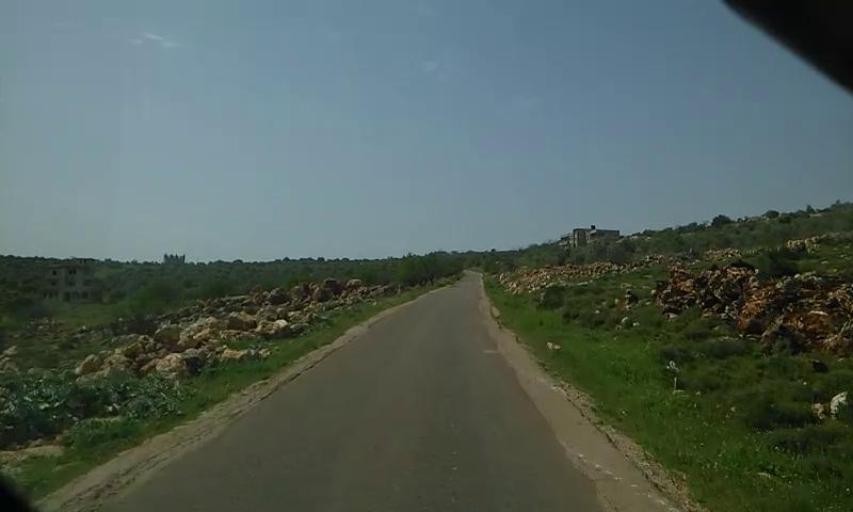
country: PS
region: West Bank
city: At Taybah
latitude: 32.4983
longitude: 35.1896
